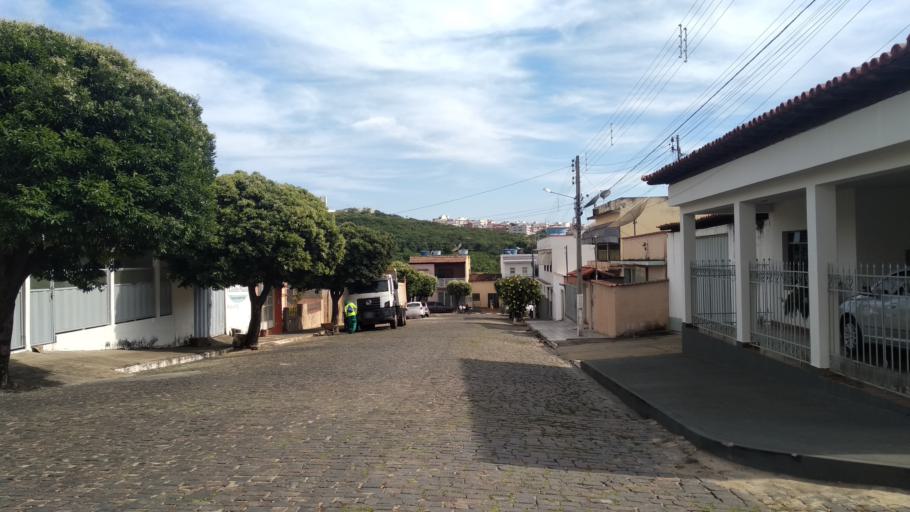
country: BR
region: Bahia
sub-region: Caetite
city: Caetite
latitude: -14.0663
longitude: -42.4935
